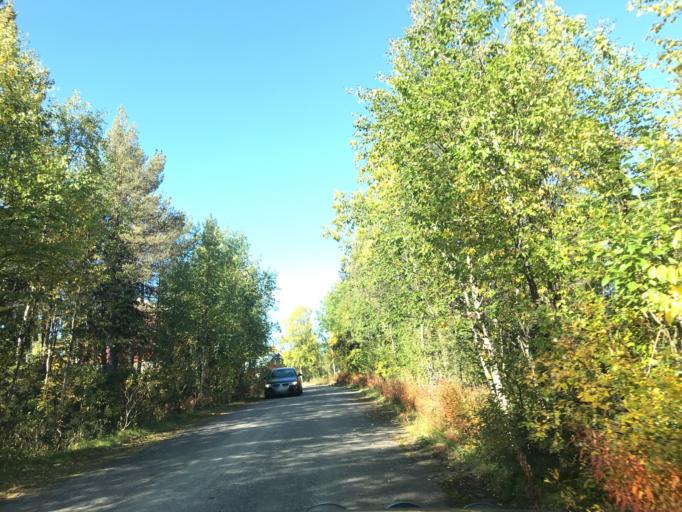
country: SE
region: Norrbotten
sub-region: Gallivare Kommun
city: Malmberget
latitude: 67.6466
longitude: 21.0718
